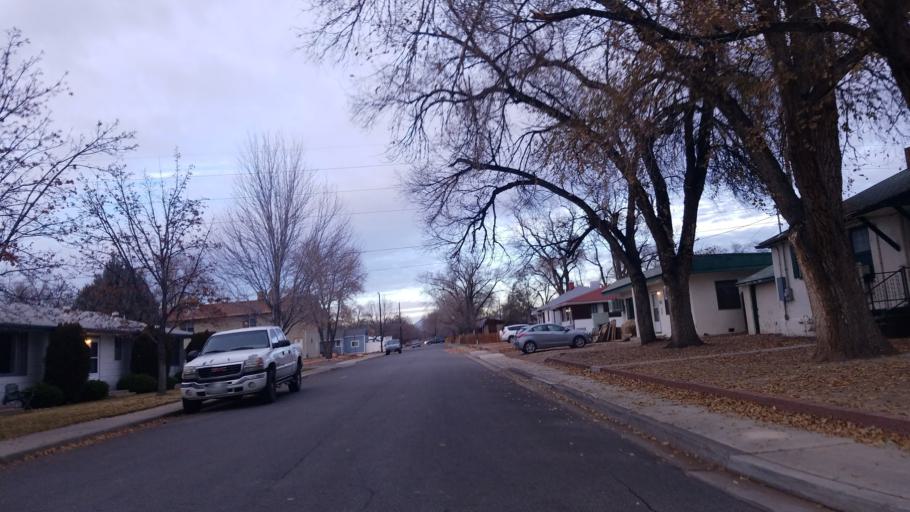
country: US
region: Colorado
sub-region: Mesa County
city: Grand Junction
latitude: 39.0684
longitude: -108.5453
